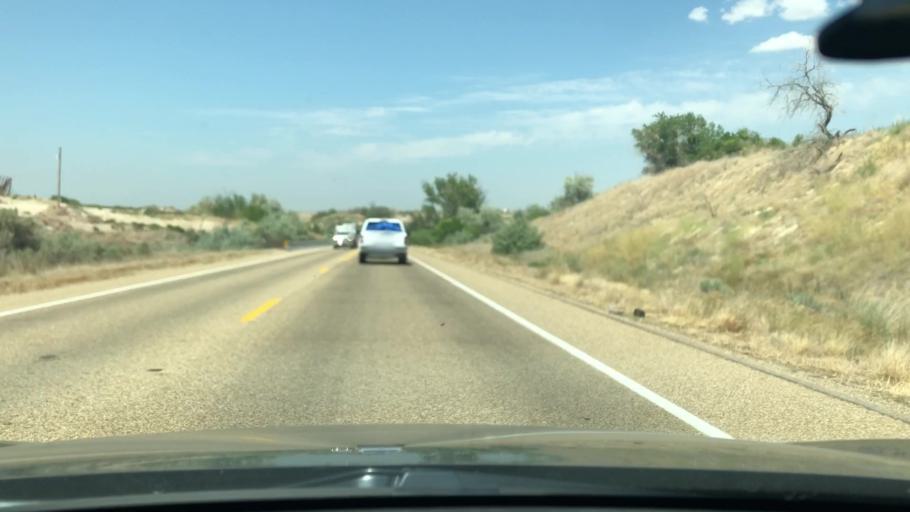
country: US
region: Idaho
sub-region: Canyon County
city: Wilder
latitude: 43.7142
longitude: -116.9118
